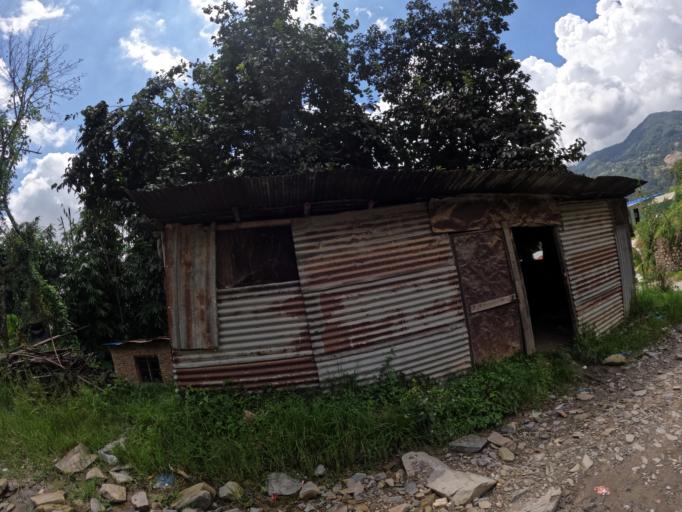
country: NP
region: Central Region
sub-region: Bagmati Zone
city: Kathmandu
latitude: 27.7889
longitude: 85.3314
